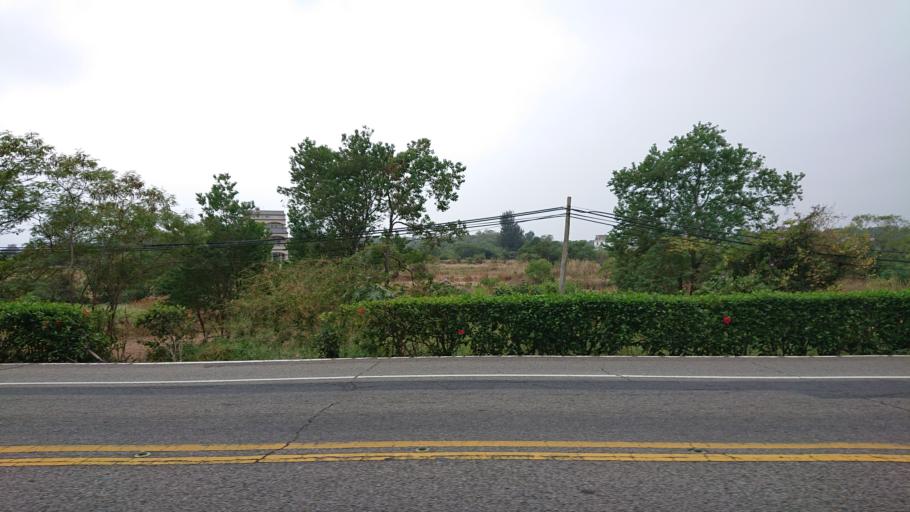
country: TW
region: Fukien
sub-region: Kinmen
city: Jincheng
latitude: 24.4446
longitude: 118.3875
